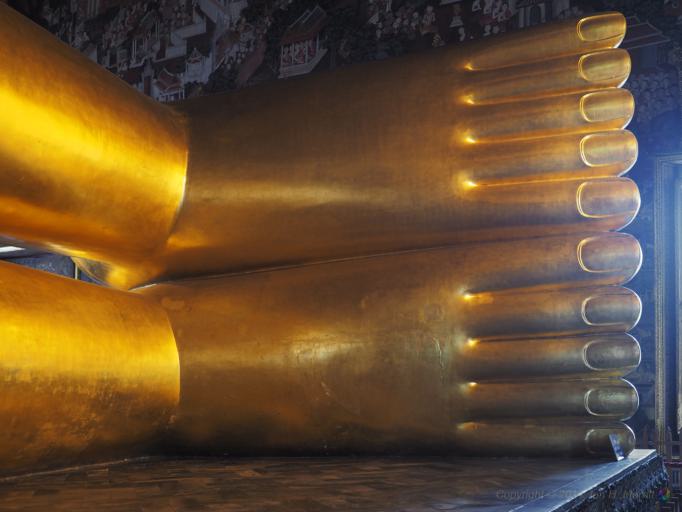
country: TH
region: Bangkok
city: Bangkok
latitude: 13.7465
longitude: 100.4933
